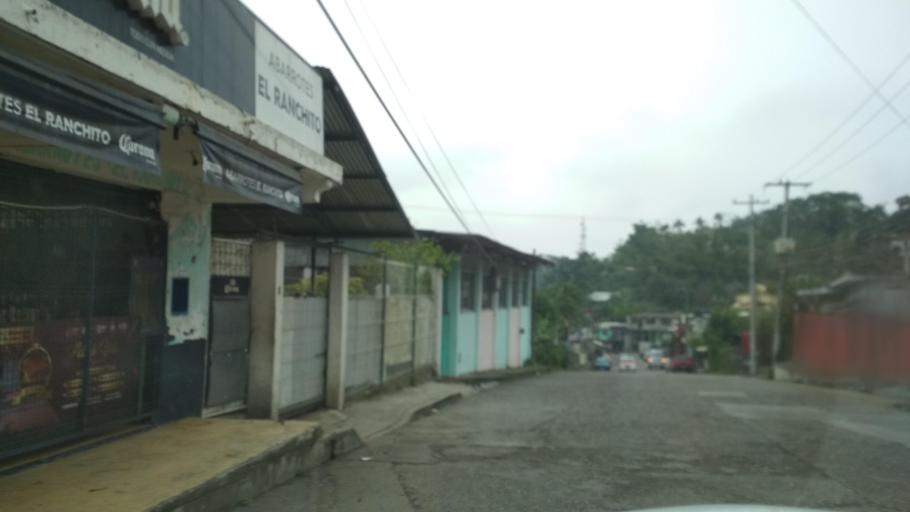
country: MX
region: Veracruz
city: Papantla de Olarte
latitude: 20.4440
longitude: -97.3120
